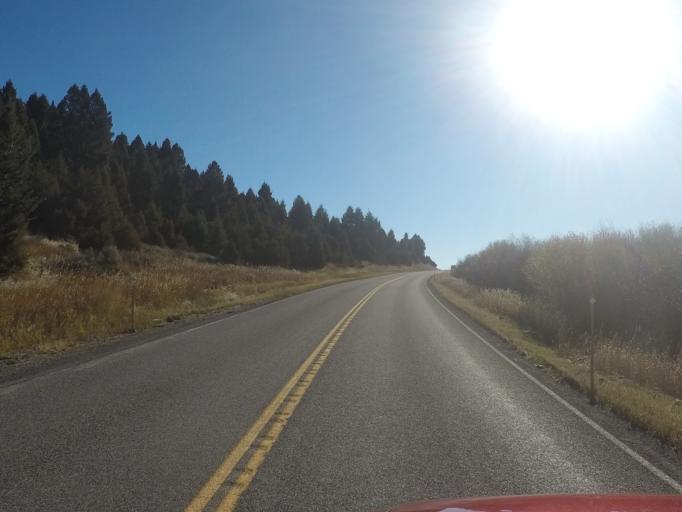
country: US
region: Montana
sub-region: Meagher County
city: White Sulphur Springs
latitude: 46.3572
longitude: -111.0898
